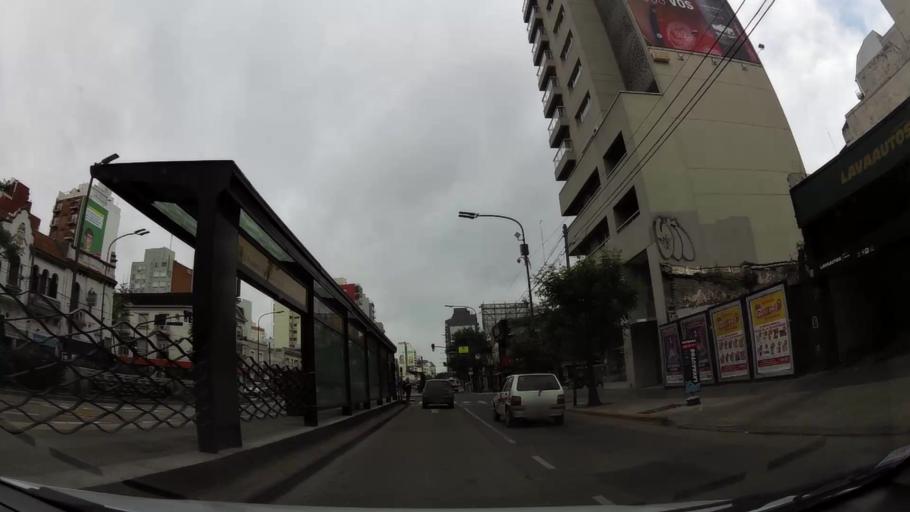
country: AR
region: Buenos Aires F.D.
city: Colegiales
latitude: -34.5492
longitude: -58.4678
